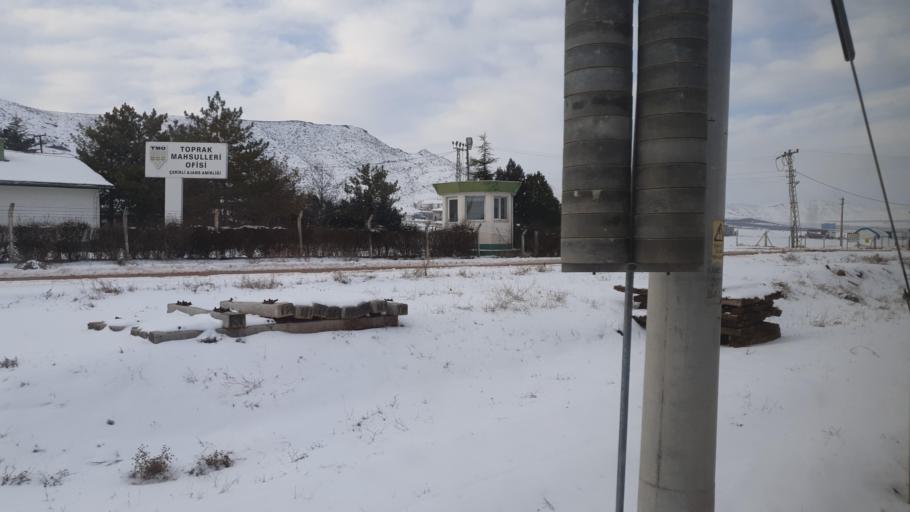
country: TR
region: Kirikkale
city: Delice
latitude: 39.8913
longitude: 33.9972
